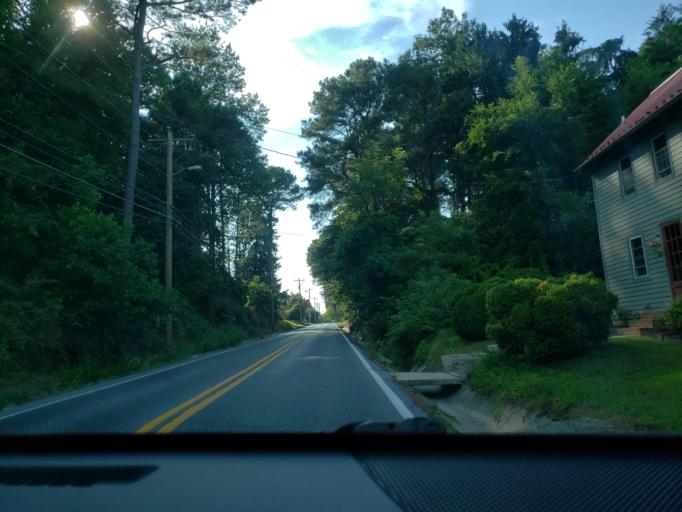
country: US
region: Delaware
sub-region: Sussex County
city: Milton
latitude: 38.7733
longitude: -75.3070
